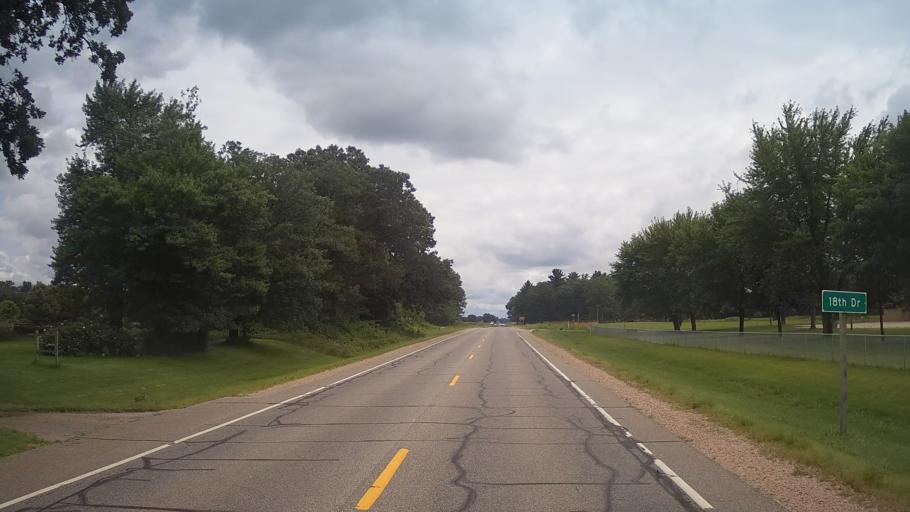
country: US
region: Wisconsin
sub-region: Adams County
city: Friendship
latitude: 44.0394
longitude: -89.9294
